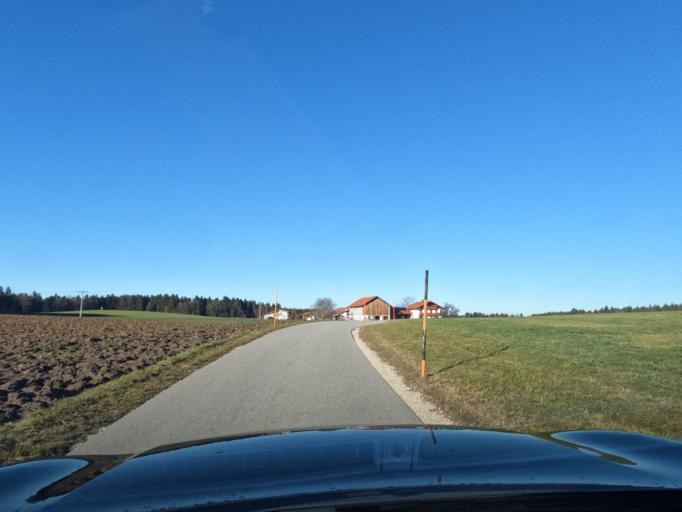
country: DE
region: Bavaria
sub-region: Upper Bavaria
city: Surberg
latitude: 47.8777
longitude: 12.6897
